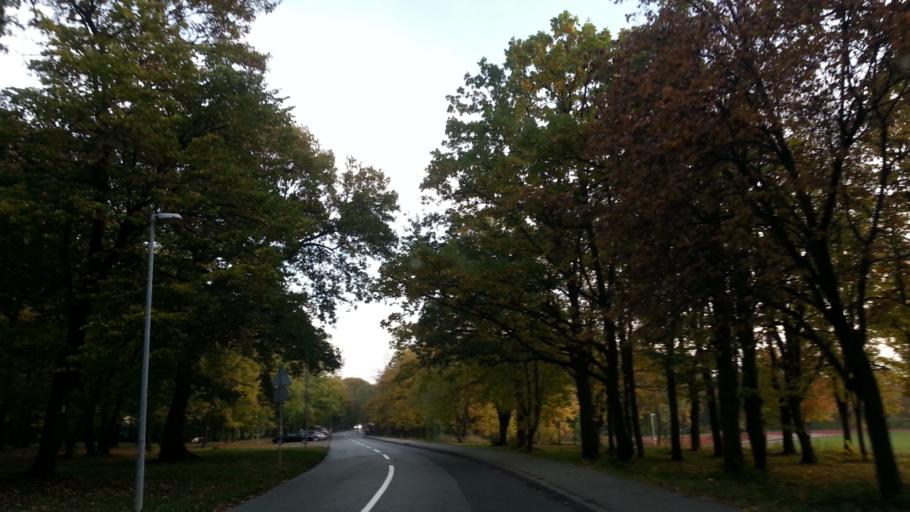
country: RS
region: Central Serbia
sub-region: Belgrade
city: Cukarica
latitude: 44.7691
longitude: 20.4273
